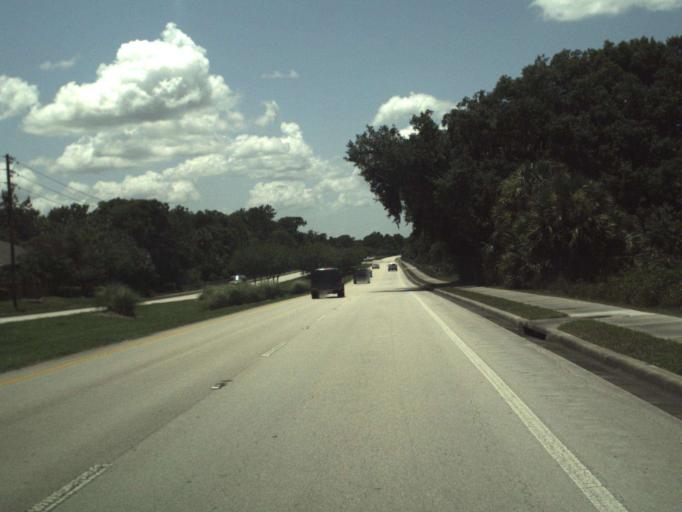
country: US
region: Florida
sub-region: Seminole County
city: Oviedo
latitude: 28.6901
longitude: -81.2457
